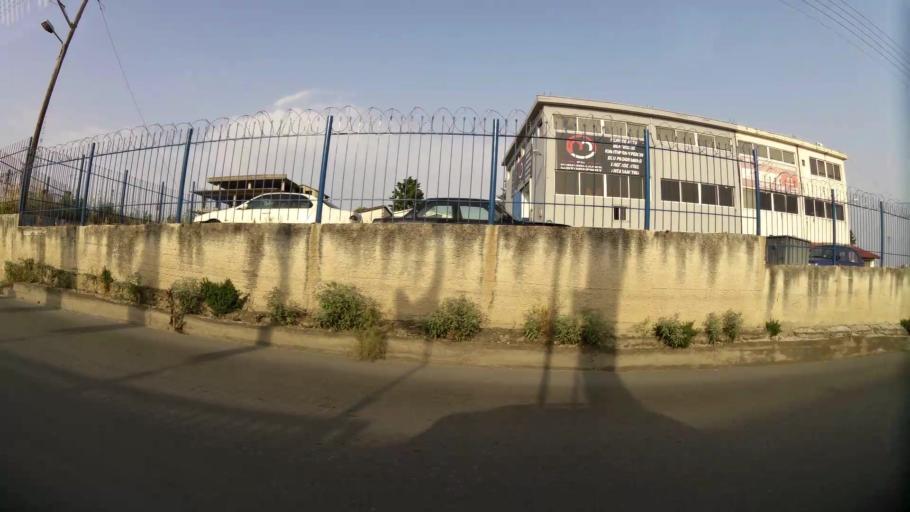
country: GR
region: Central Macedonia
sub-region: Nomos Thessalonikis
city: Evosmos
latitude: 40.6865
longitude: 22.9061
